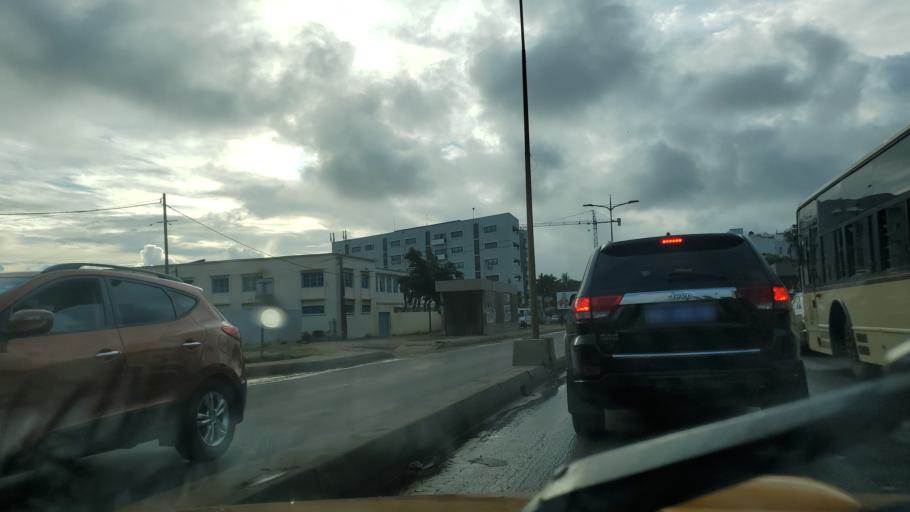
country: SN
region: Dakar
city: Mermoz Boabab
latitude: 14.7159
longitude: -17.4831
